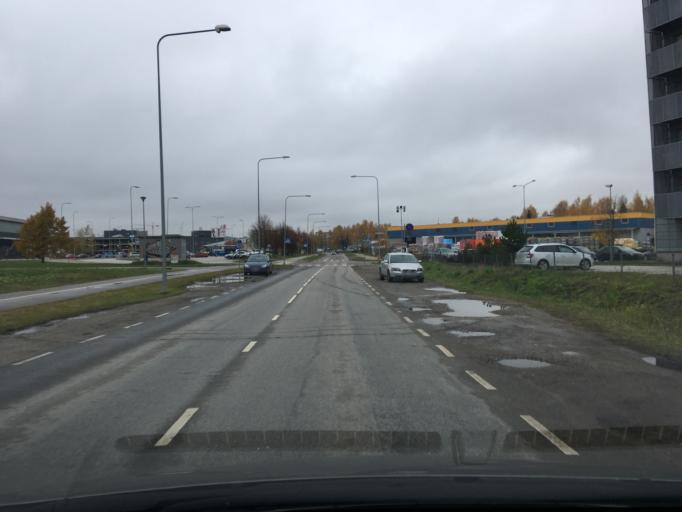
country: EE
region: Tartu
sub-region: Tartu linn
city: Tartu
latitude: 58.3703
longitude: 26.7556
